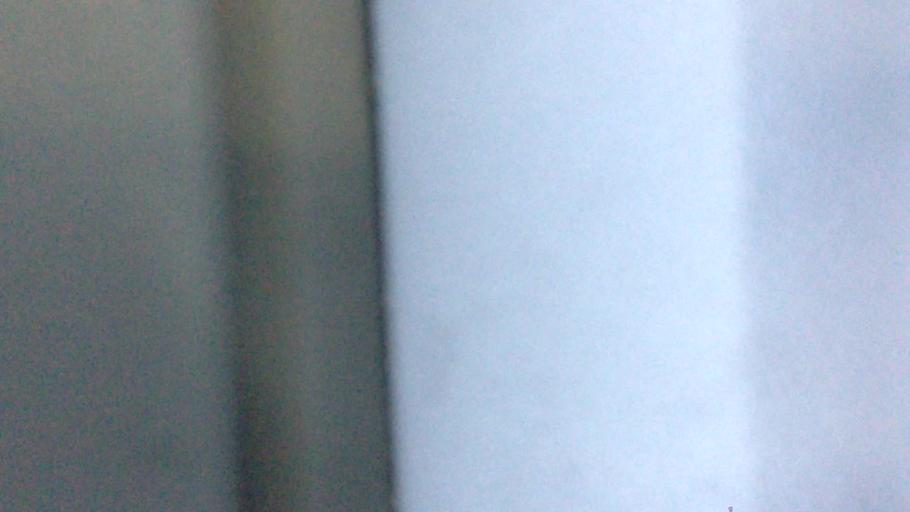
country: US
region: New York
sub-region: Dutchess County
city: Rhinebeck
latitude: 41.9525
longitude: -73.9184
